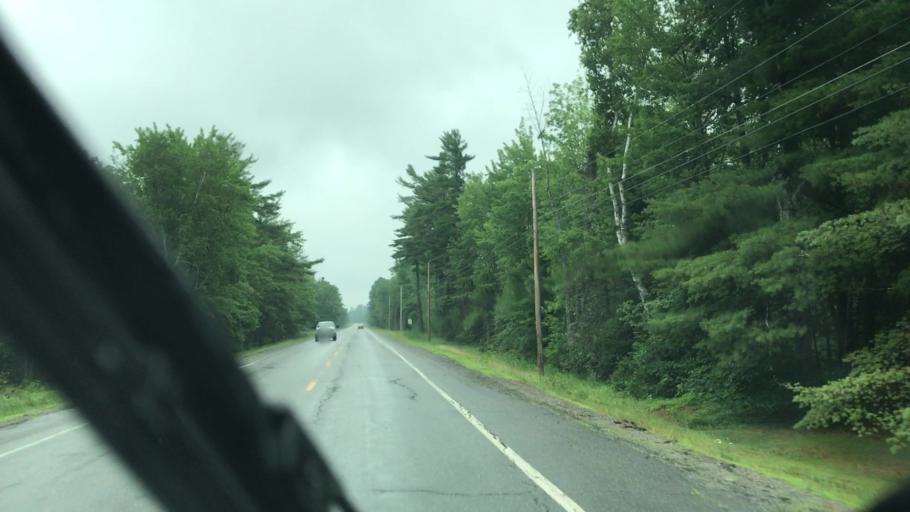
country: US
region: Maine
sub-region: Penobscot County
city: Howland
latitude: 45.2407
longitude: -68.6416
